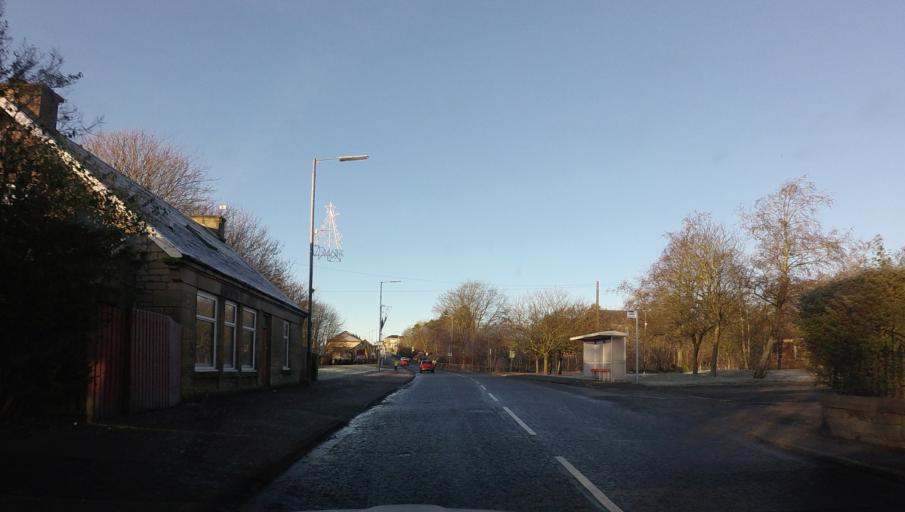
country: GB
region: Scotland
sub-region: North Lanarkshire
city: Shotts
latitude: 55.8182
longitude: -3.7930
